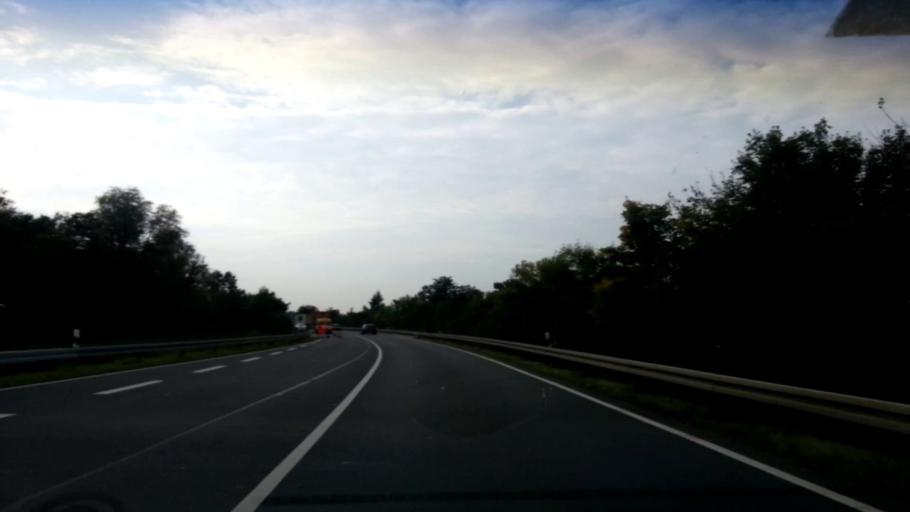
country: DE
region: Bavaria
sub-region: Regierungsbezirk Unterfranken
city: Prichsenstadt
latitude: 49.8455
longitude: 10.3510
